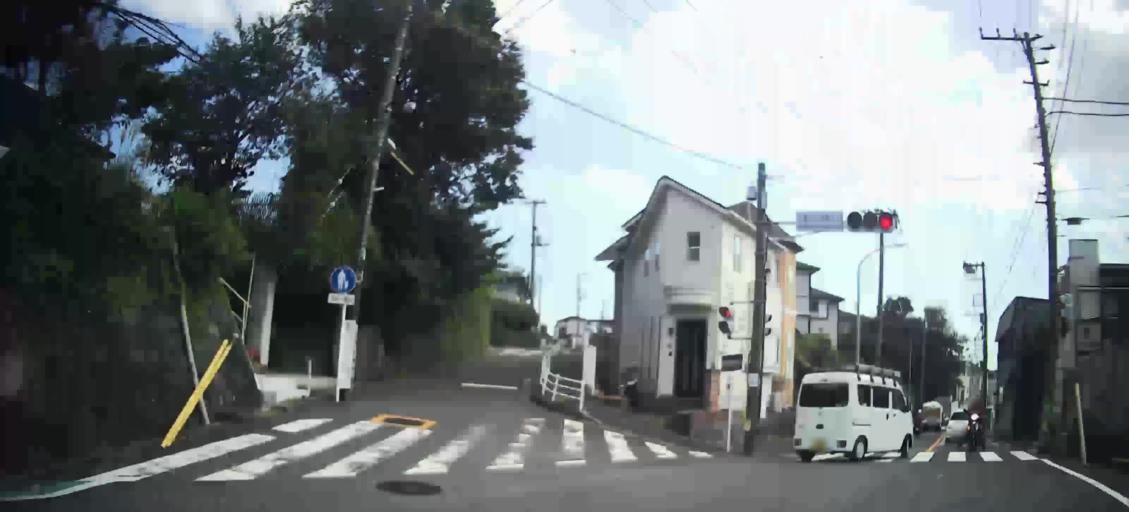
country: JP
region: Kanagawa
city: Yokohama
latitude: 35.4806
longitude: 139.5771
